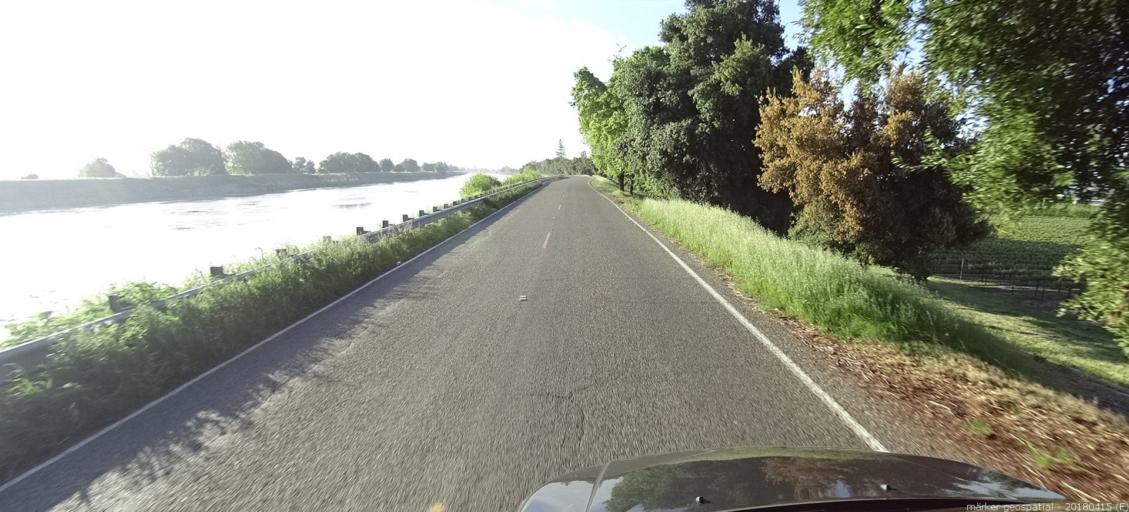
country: US
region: California
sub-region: Sacramento County
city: Walnut Grove
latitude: 38.2994
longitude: -121.5698
